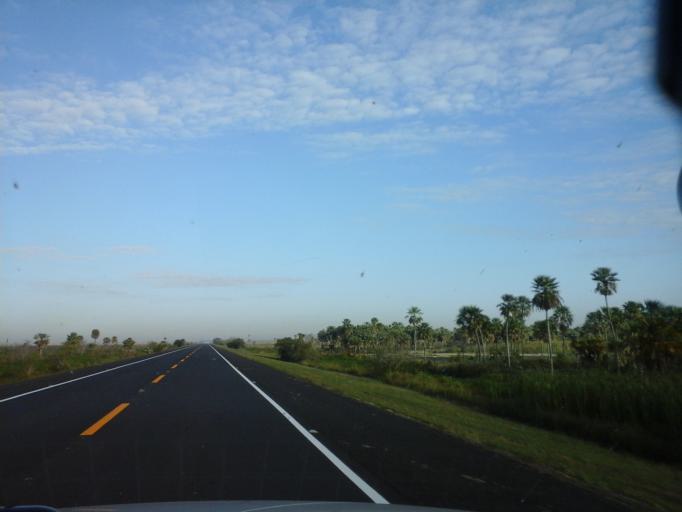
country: PY
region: Neembucu
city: Cerrito
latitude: -26.8680
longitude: -57.7674
